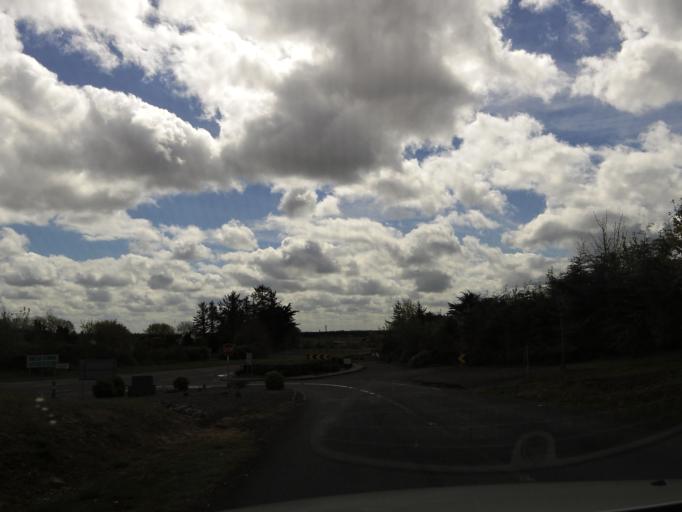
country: IE
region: Connaught
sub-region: Maigh Eo
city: Claremorris
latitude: 53.7562
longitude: -8.9649
